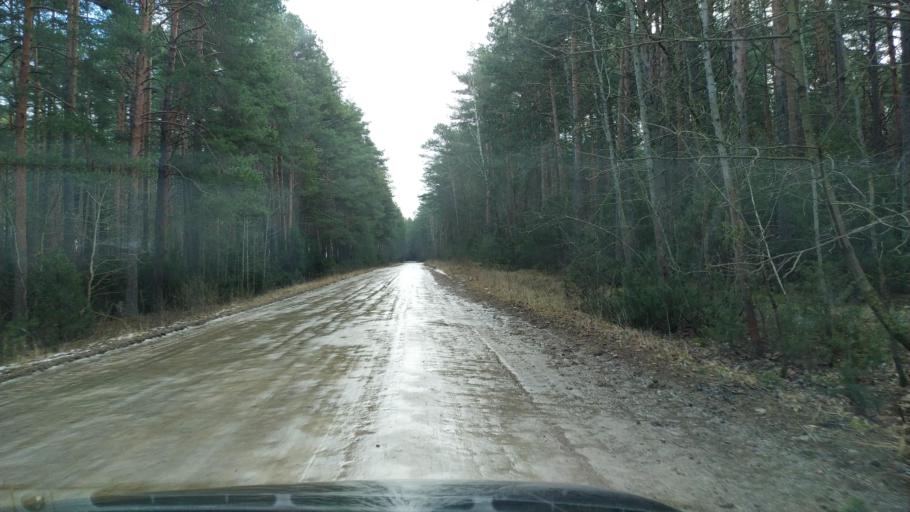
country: BY
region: Brest
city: Kamyanyets
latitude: 52.4269
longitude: 23.9873
